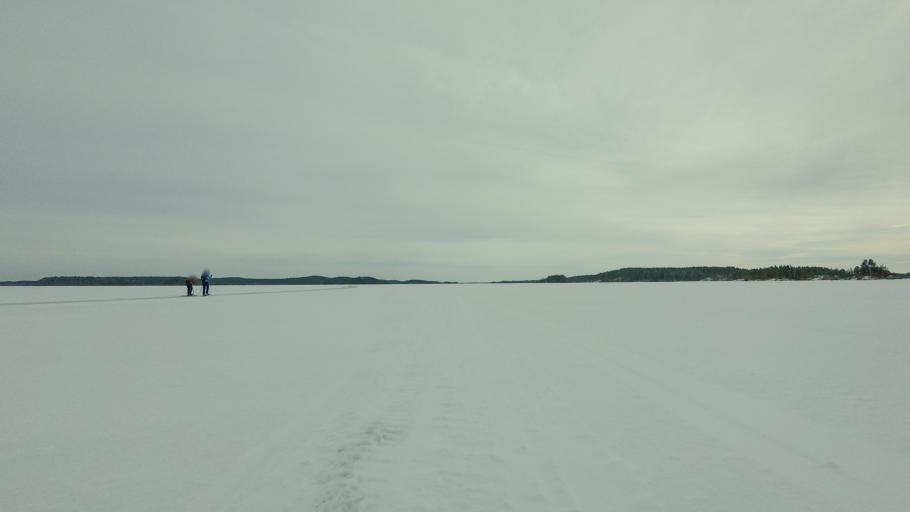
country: FI
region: Southern Savonia
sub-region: Savonlinna
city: Rantasalmi
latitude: 62.1027
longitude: 28.4325
